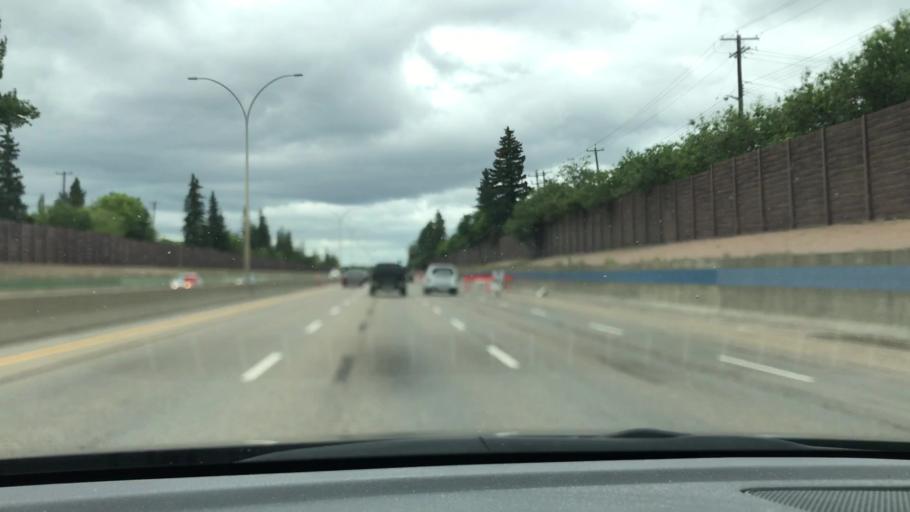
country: CA
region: Alberta
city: Edmonton
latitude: 53.4833
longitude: -113.5274
